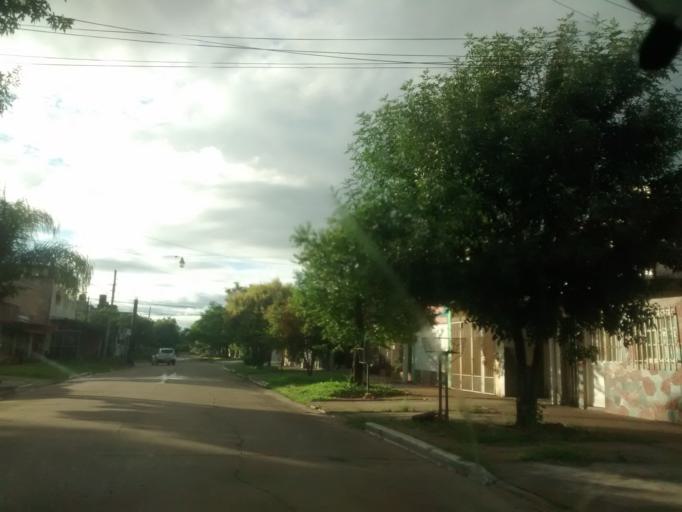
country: AR
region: Chaco
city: Resistencia
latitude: -27.4640
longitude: -58.9737
